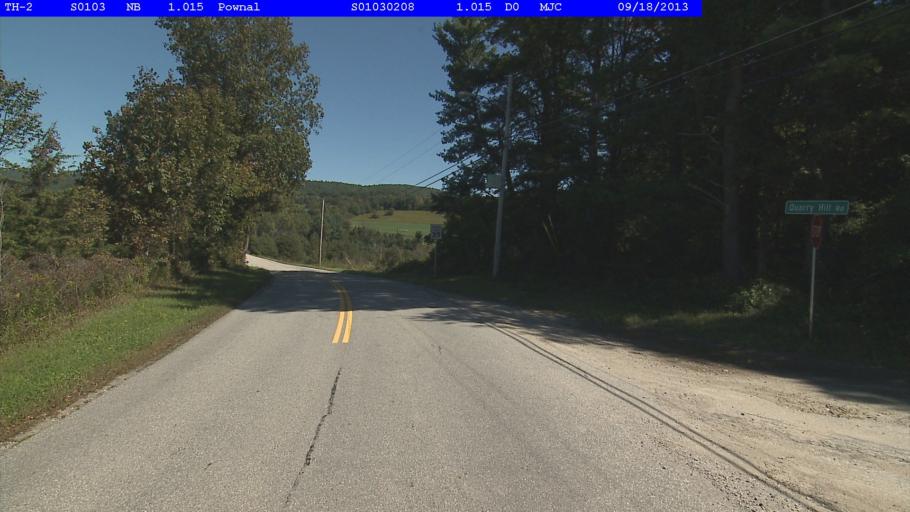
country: US
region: Vermont
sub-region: Bennington County
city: Bennington
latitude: 42.8017
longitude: -73.2503
